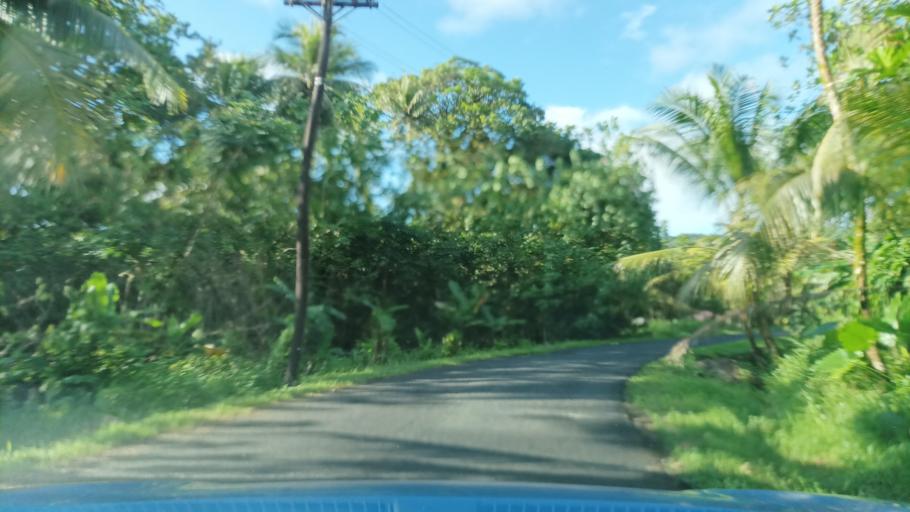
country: FM
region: Pohnpei
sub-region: Kolonia Municipality
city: Kolonia Town
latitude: 6.9578
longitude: 158.1850
